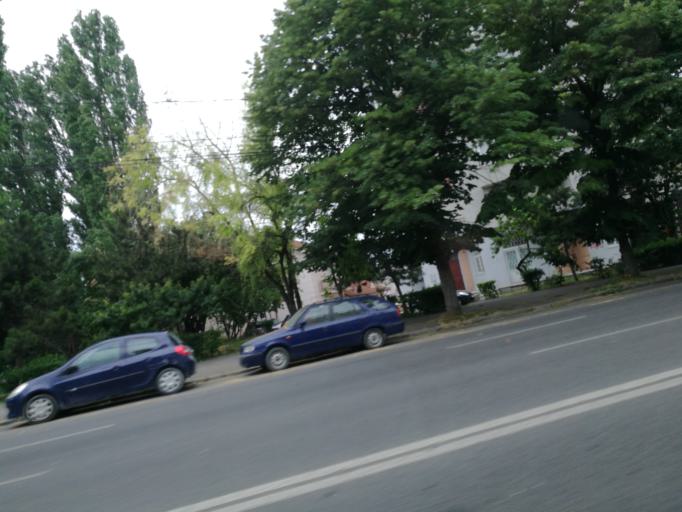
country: RO
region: Constanta
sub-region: Municipiul Constanta
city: Constanta
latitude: 44.1858
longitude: 28.6350
